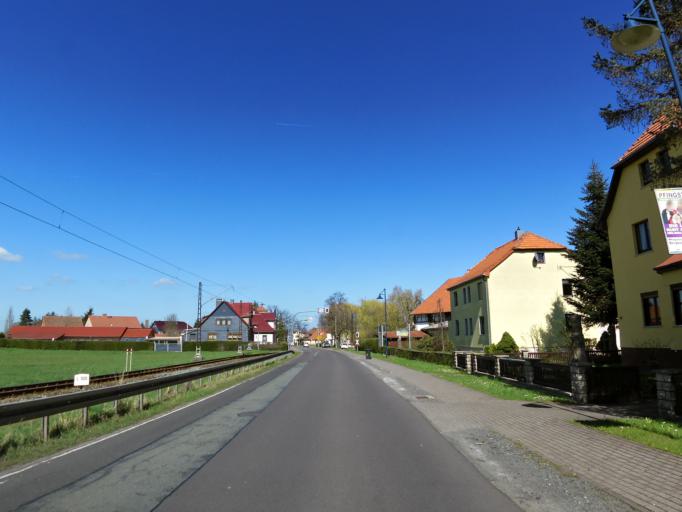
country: DE
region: Thuringia
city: Horselgau
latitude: 50.8984
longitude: 10.5969
